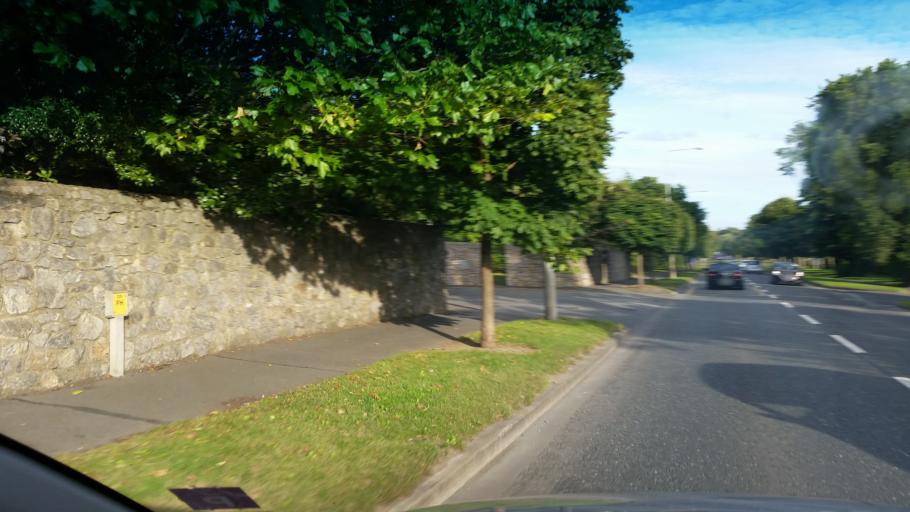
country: IE
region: Leinster
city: Kinsealy-Drinan
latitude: 53.4493
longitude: -6.1829
